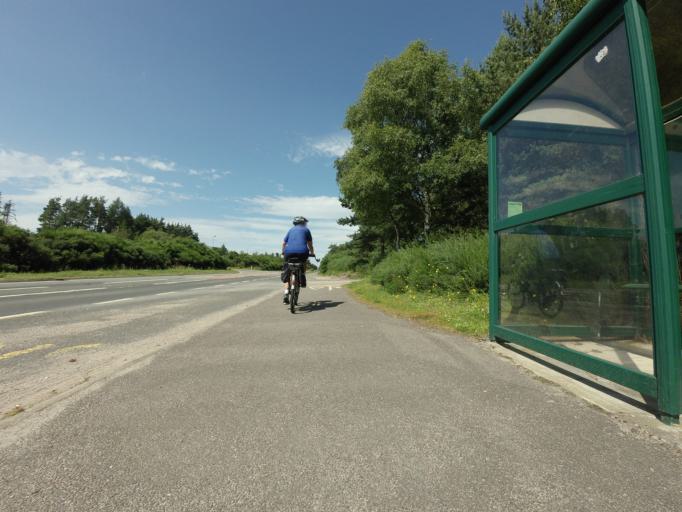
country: GB
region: Scotland
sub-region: Highland
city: Conon Bridge
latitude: 57.5414
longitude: -4.3751
